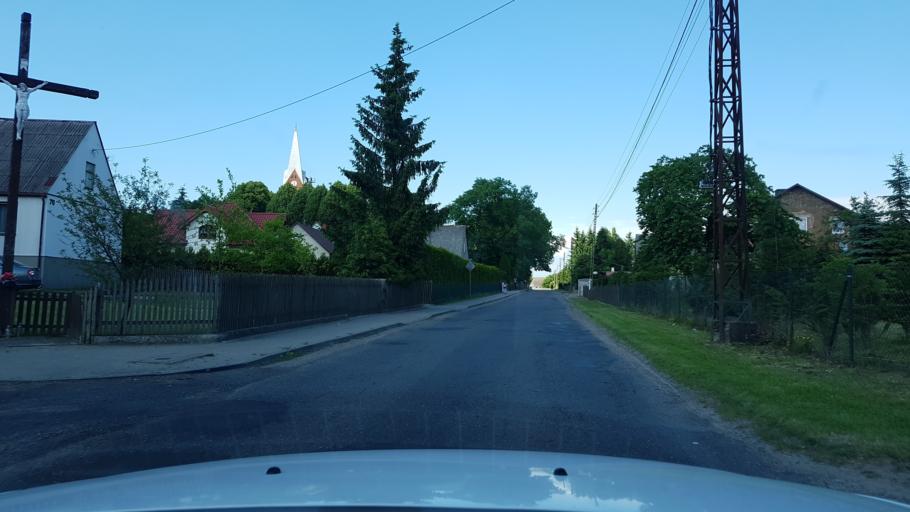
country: PL
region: West Pomeranian Voivodeship
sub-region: Powiat gryfinski
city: Banie
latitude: 53.0388
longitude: 14.6246
